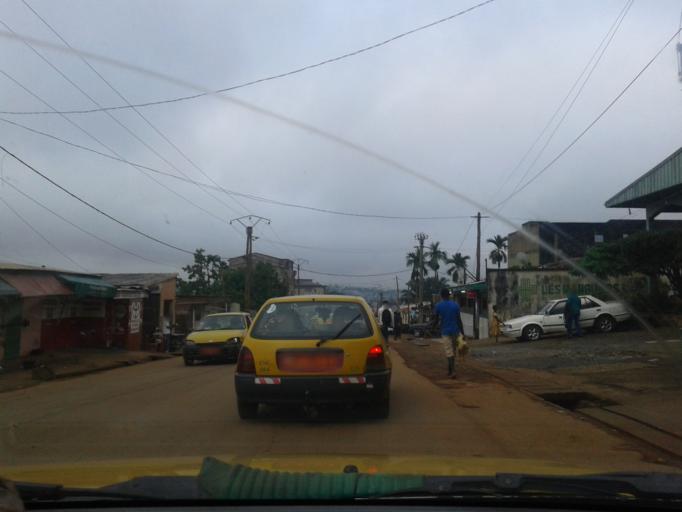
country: CM
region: Centre
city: Yaounde
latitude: 3.8986
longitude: 11.5319
